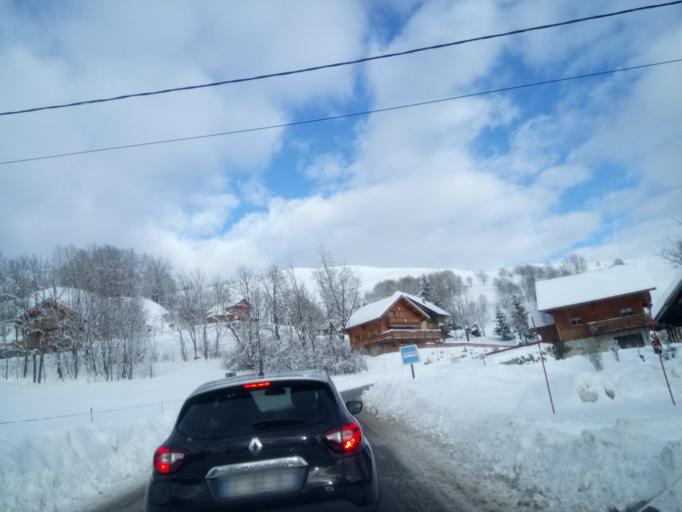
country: FR
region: Rhone-Alpes
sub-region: Departement de la Savoie
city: Saint-Jean-de-Maurienne
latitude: 45.2562
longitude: 6.2909
